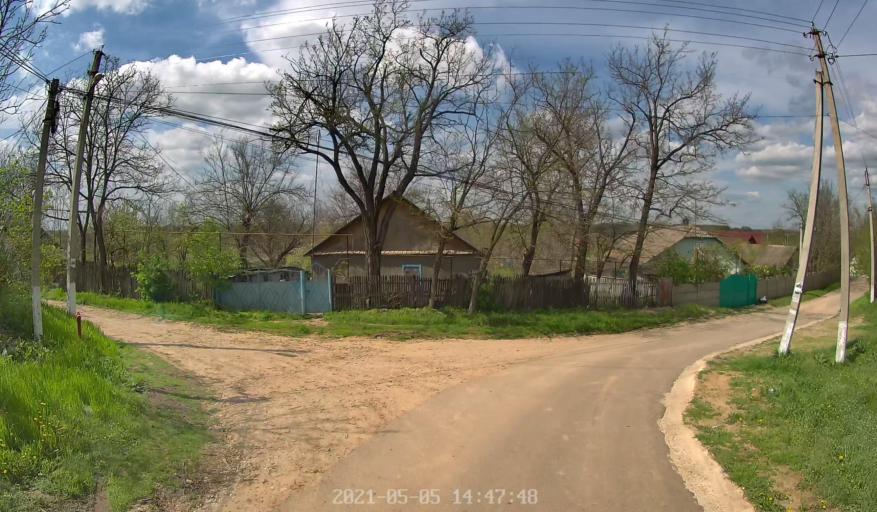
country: MD
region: Chisinau
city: Vadul lui Voda
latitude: 47.0987
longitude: 29.1685
